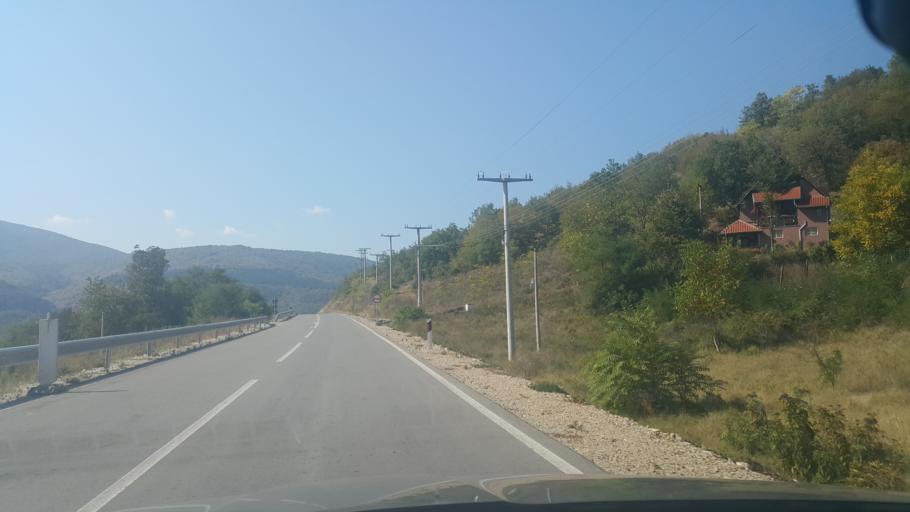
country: RS
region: Central Serbia
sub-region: Pirotski Okrug
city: Pirot
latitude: 43.2151
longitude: 22.5145
